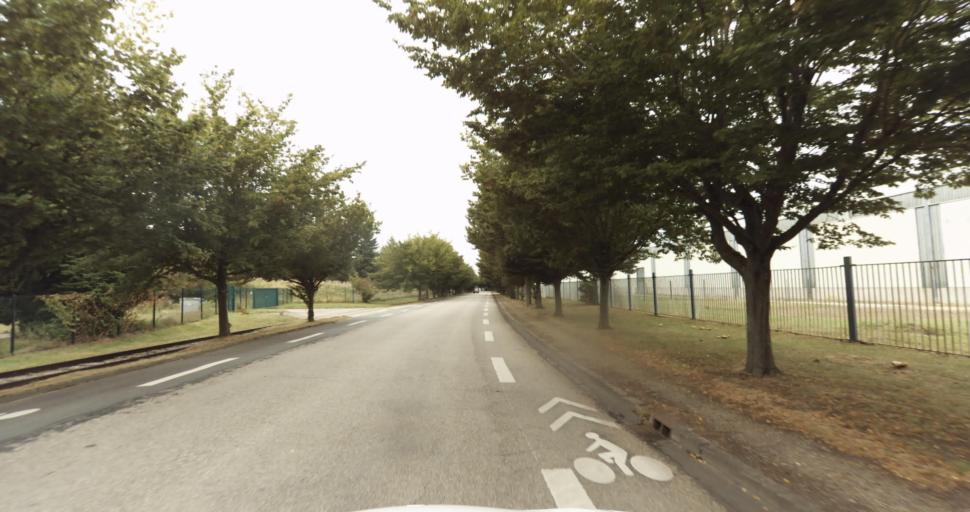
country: FR
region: Haute-Normandie
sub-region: Departement de l'Eure
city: Evreux
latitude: 49.0192
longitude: 1.1768
